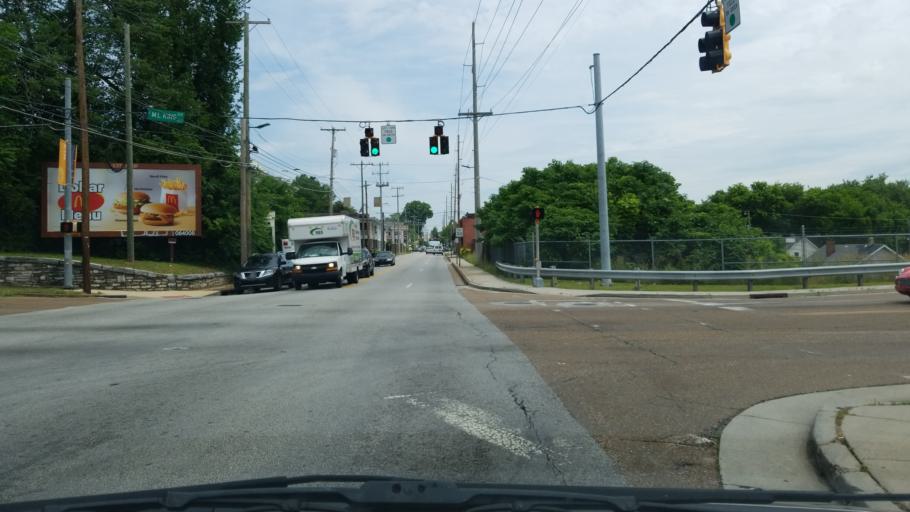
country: US
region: Tennessee
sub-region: Hamilton County
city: Chattanooga
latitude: 35.0396
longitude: -85.2921
